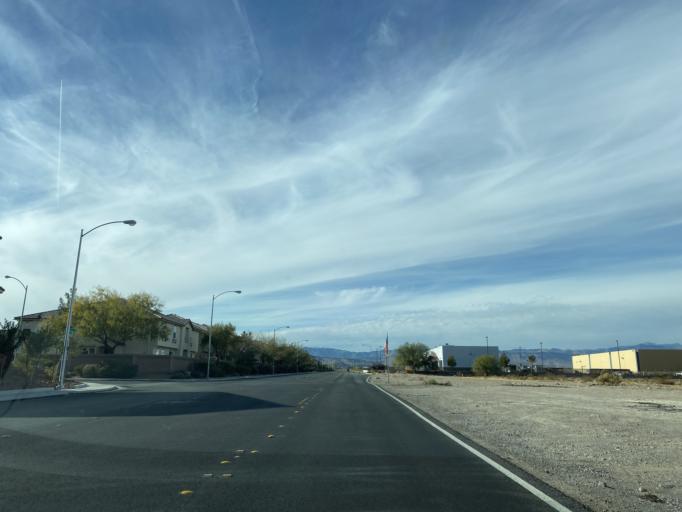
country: US
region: Nevada
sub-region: Clark County
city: Enterprise
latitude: 36.0619
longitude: -115.2264
